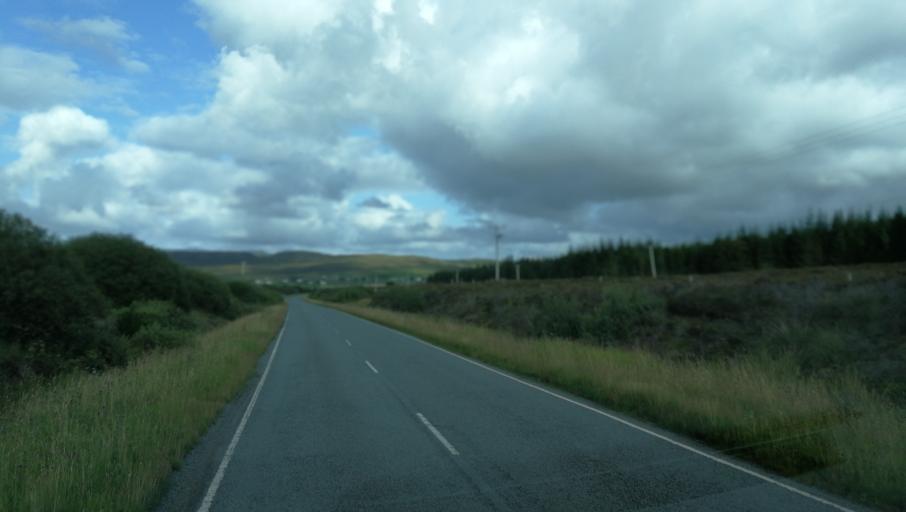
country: GB
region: Scotland
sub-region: Highland
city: Isle of Skye
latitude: 57.4716
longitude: -6.4604
